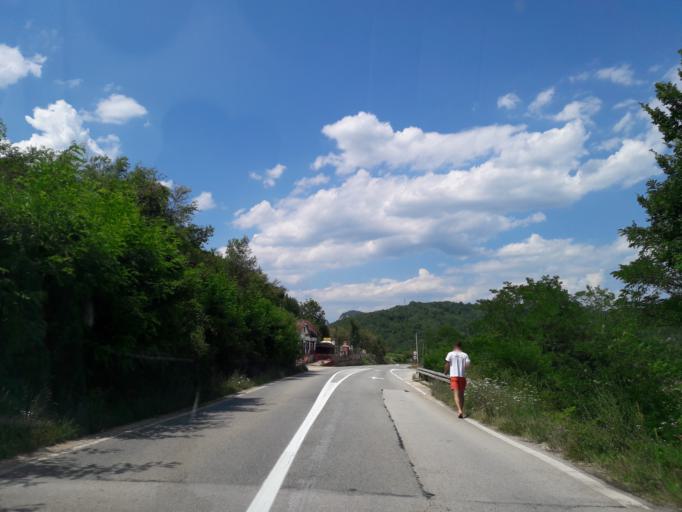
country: BA
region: Republika Srpska
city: Mrkonjic Grad
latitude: 44.5348
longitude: 17.1497
